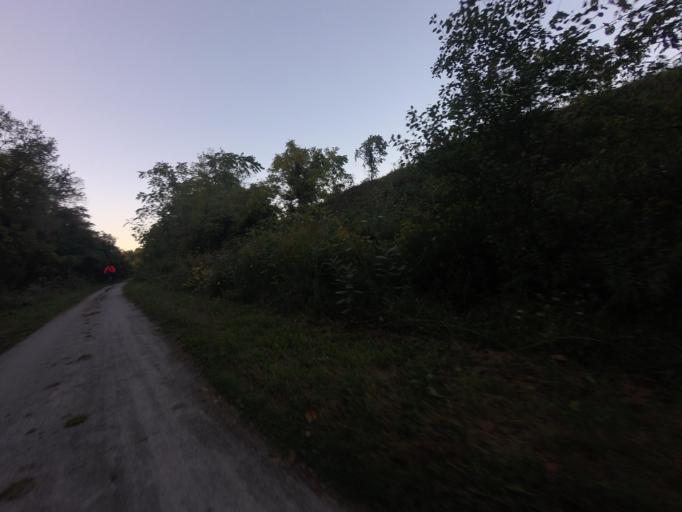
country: CA
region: Ontario
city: Brampton
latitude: 43.9145
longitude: -79.8407
